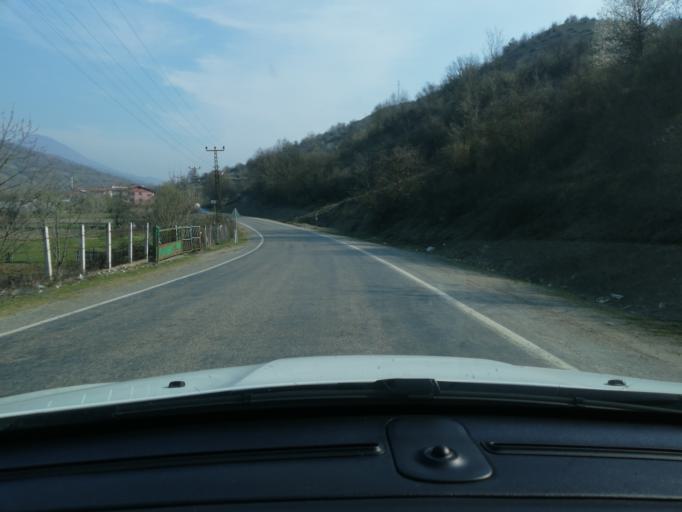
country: TR
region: Karabuk
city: Yenice
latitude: 41.2478
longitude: 32.3573
